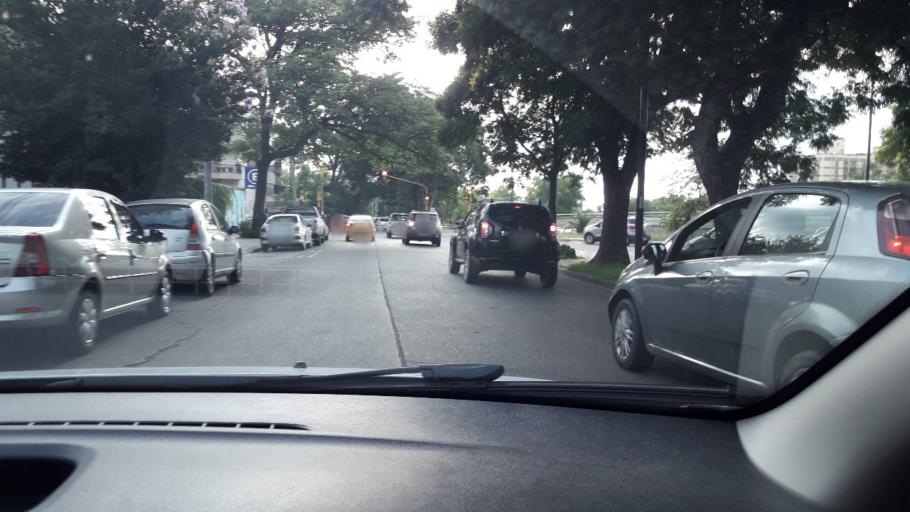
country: AR
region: Jujuy
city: San Salvador de Jujuy
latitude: -24.1888
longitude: -65.2967
